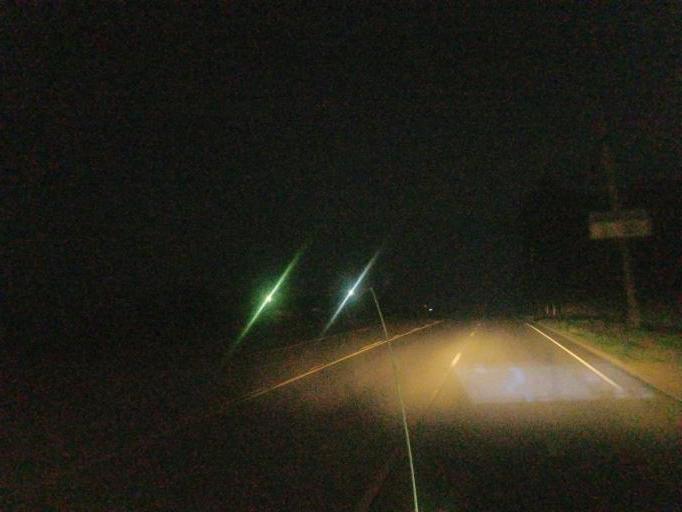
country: US
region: Kentucky
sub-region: Barren County
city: Glasgow
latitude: 36.9780
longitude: -85.8902
